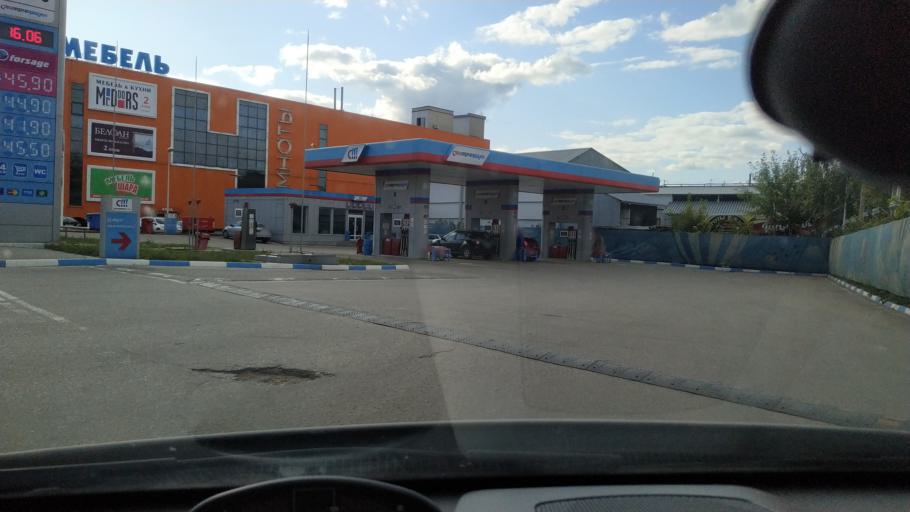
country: RU
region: Rjazan
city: Ryazan'
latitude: 54.6197
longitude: 39.6993
